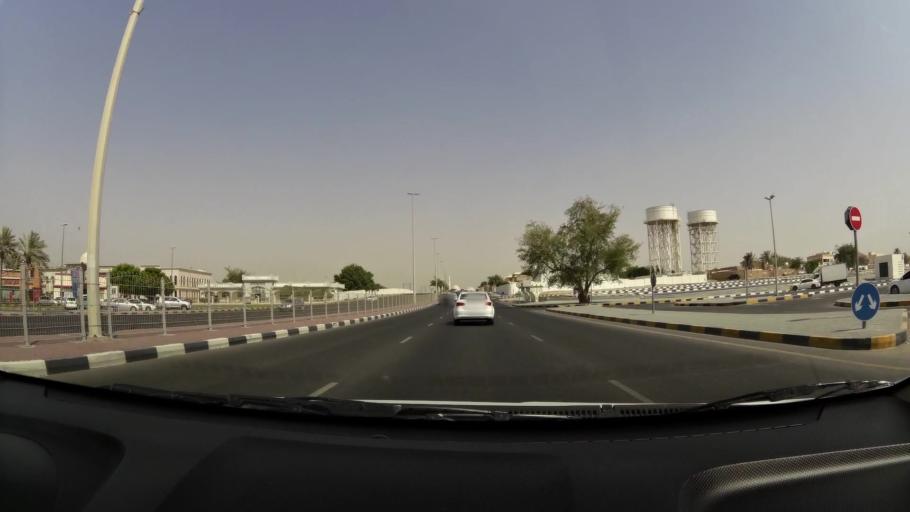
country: AE
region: Ash Shariqah
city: Sharjah
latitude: 25.3454
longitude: 55.4219
